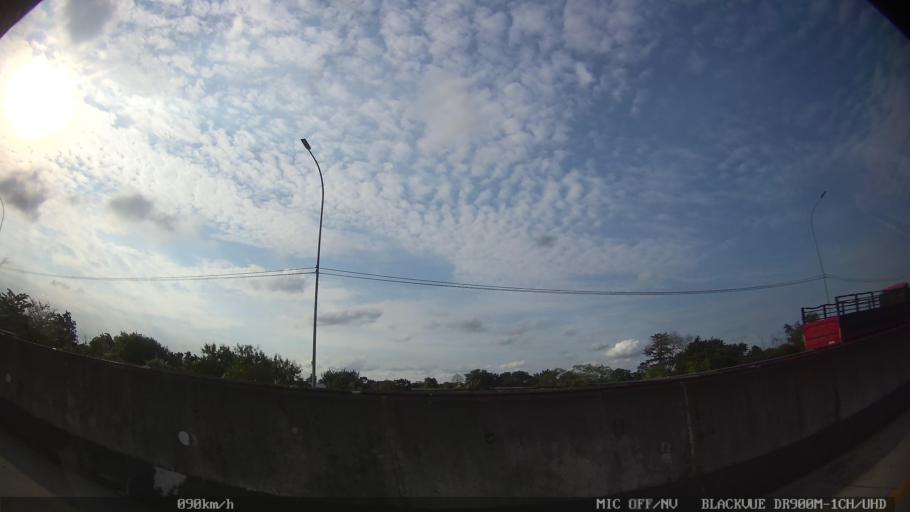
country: ID
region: North Sumatra
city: Medan
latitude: 3.6488
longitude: 98.6554
